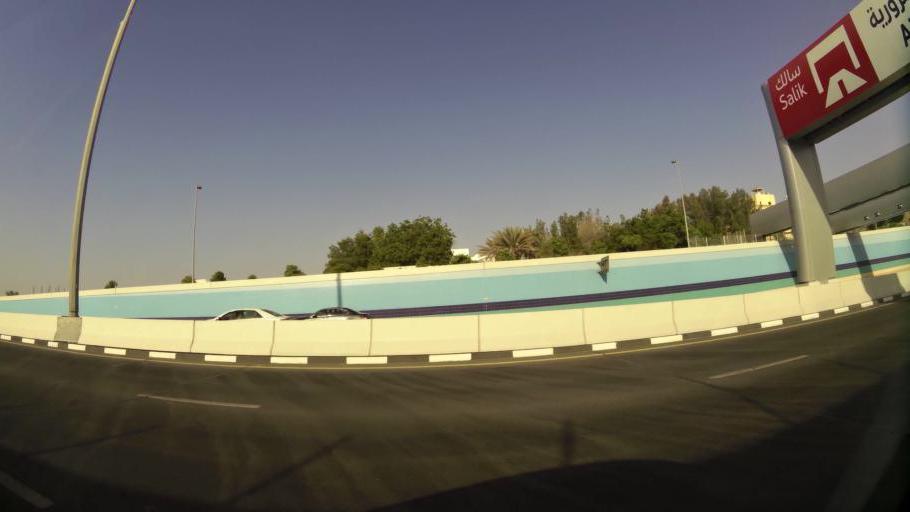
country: AE
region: Ash Shariqah
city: Sharjah
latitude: 25.2493
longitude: 55.3871
